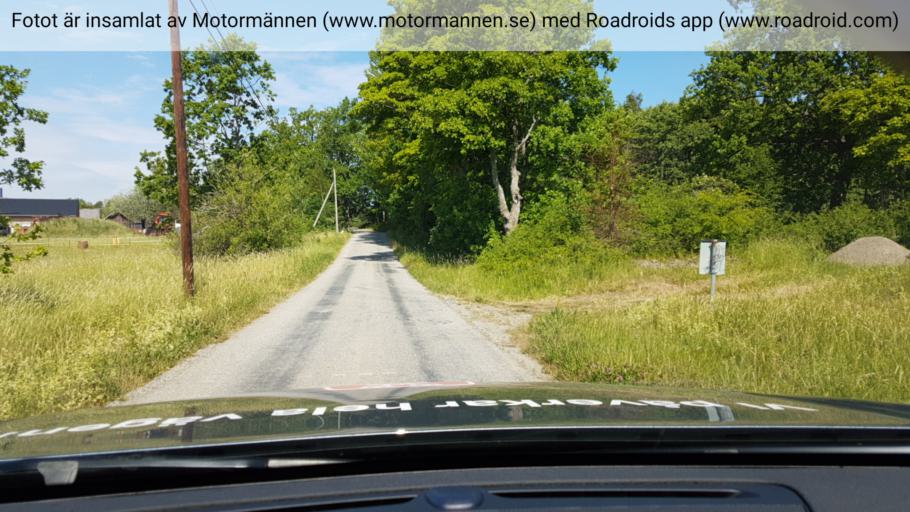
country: SE
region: Stockholm
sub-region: Haninge Kommun
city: Jordbro
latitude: 59.0120
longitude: 18.1175
